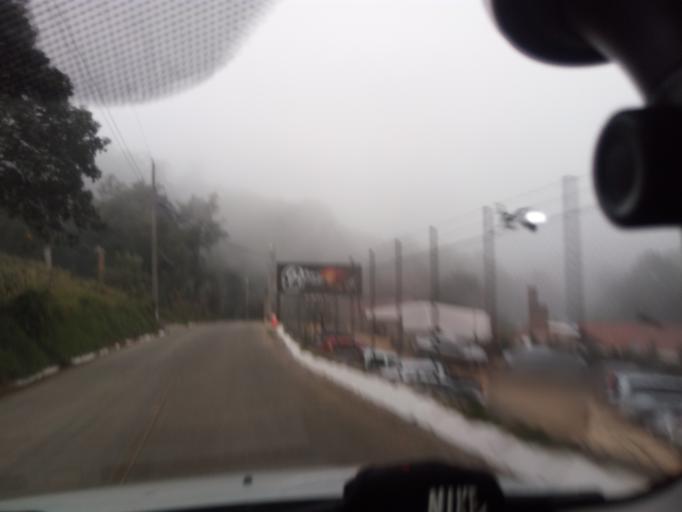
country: GT
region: Sacatepequez
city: San Bartolome Milpas Altas
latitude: 14.5928
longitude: -90.7038
